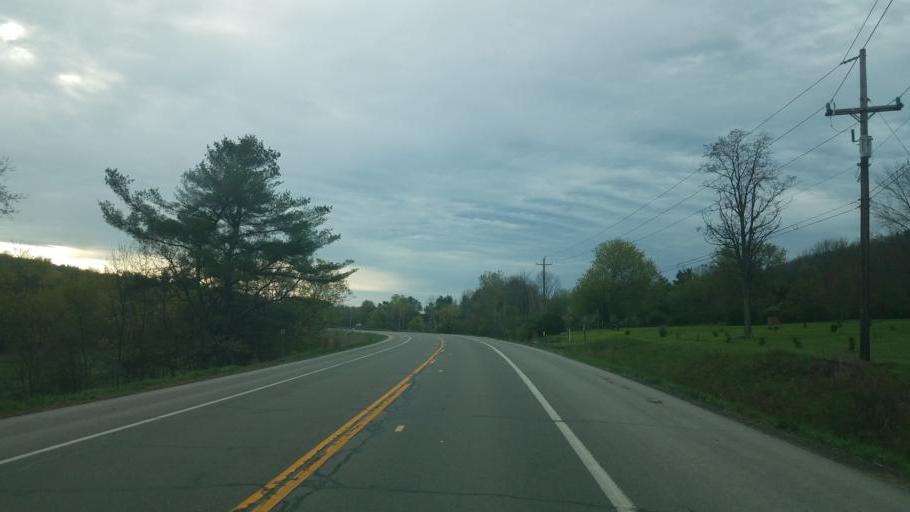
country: US
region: Pennsylvania
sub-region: Tioga County
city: Westfield
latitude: 42.1102
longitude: -77.4826
